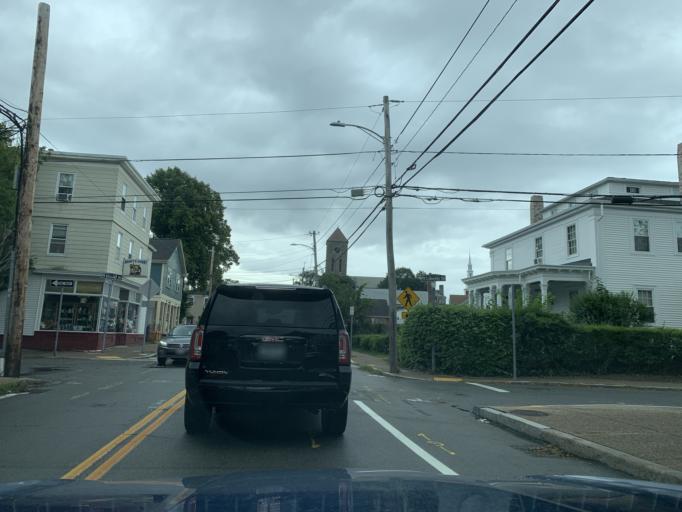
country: US
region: Rhode Island
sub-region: Bristol County
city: Warren
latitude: 41.7323
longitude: -71.2830
